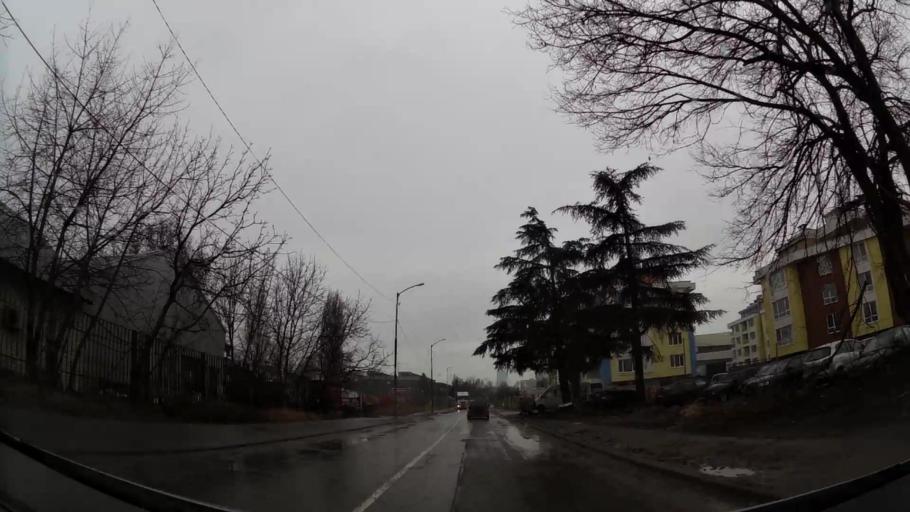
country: BG
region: Sofia-Capital
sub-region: Stolichna Obshtina
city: Sofia
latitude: 42.6638
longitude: 23.4057
